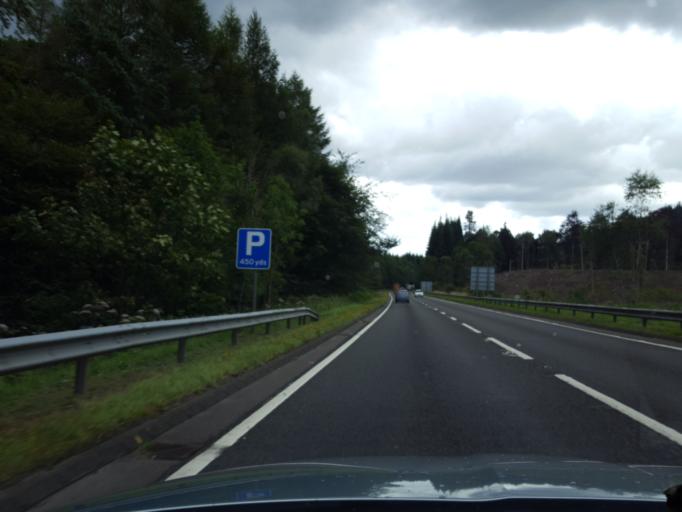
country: GB
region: Scotland
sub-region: Perth and Kinross
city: Bankfoot
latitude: 56.5488
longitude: -3.5600
